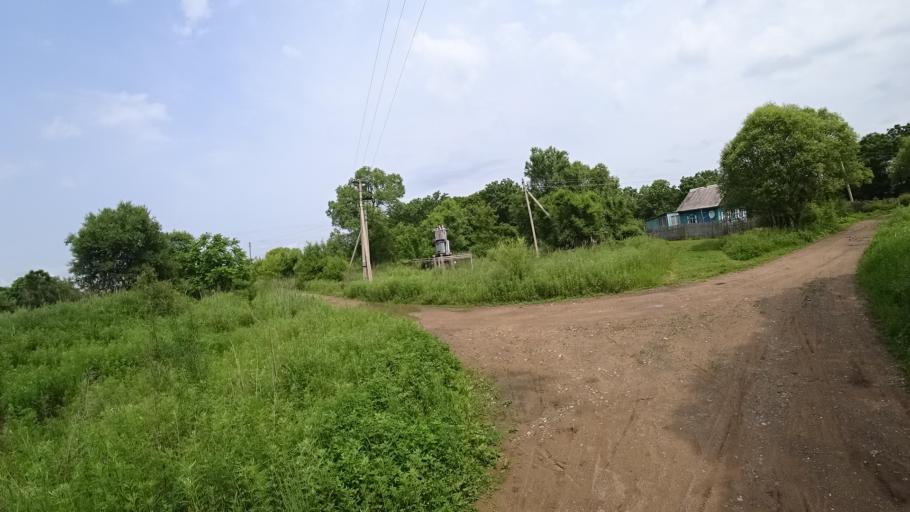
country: RU
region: Primorskiy
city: Novosysoyevka
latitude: 44.2473
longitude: 133.3696
